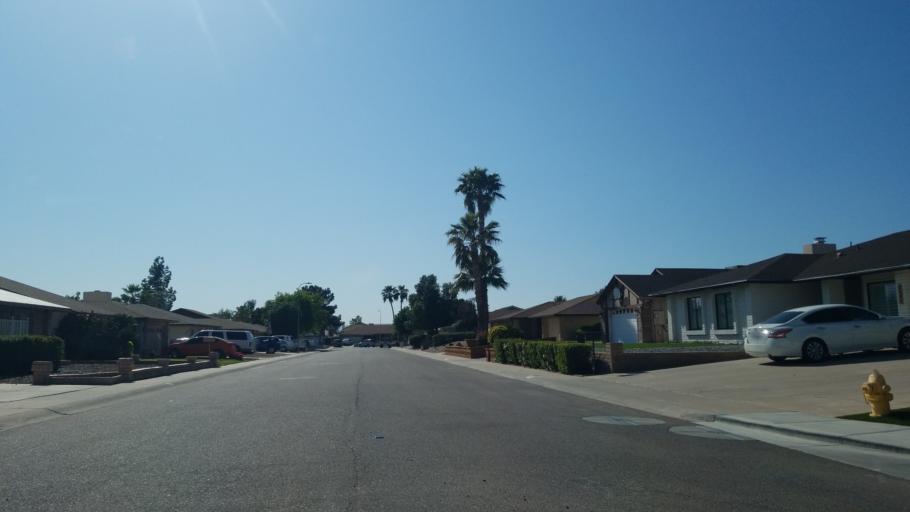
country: US
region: Arizona
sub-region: Maricopa County
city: Glendale
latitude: 33.5814
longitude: -112.1775
